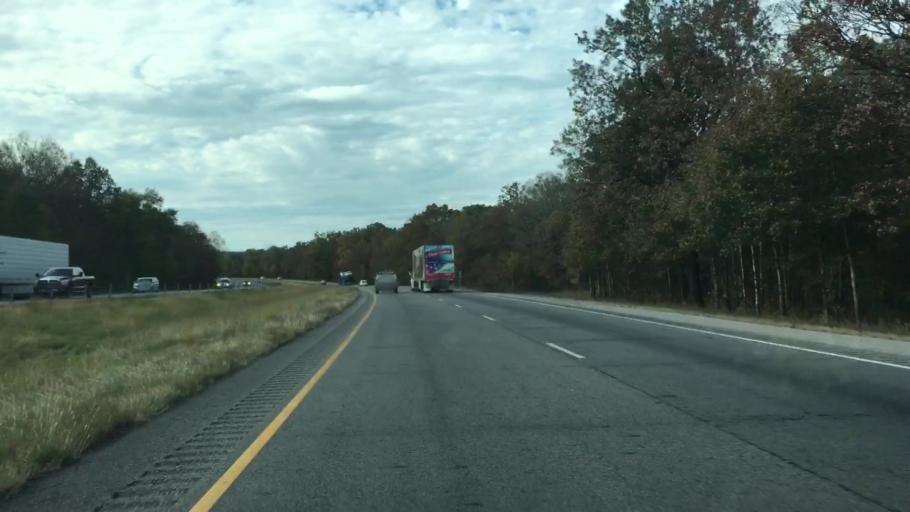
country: US
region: Arkansas
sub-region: Pope County
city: Atkins
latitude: 35.2447
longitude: -92.8640
